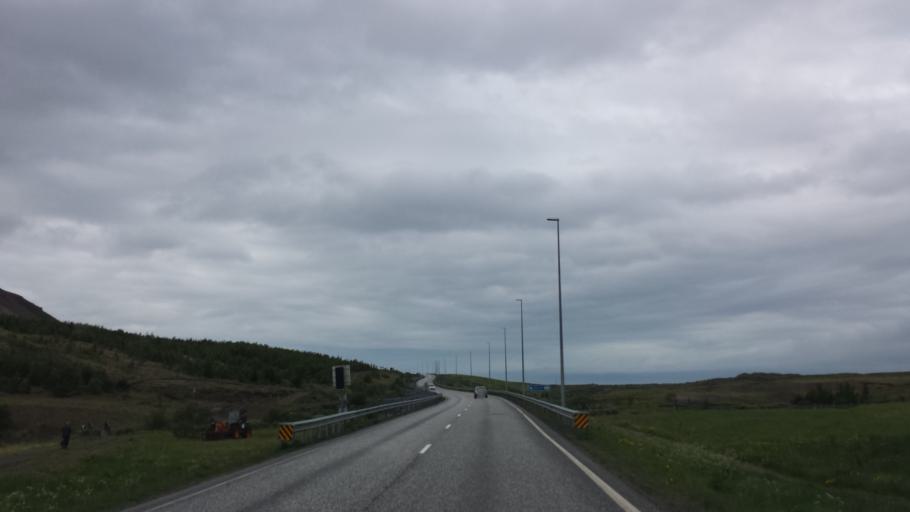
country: IS
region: Capital Region
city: Mosfellsbaer
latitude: 64.1803
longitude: -21.6421
